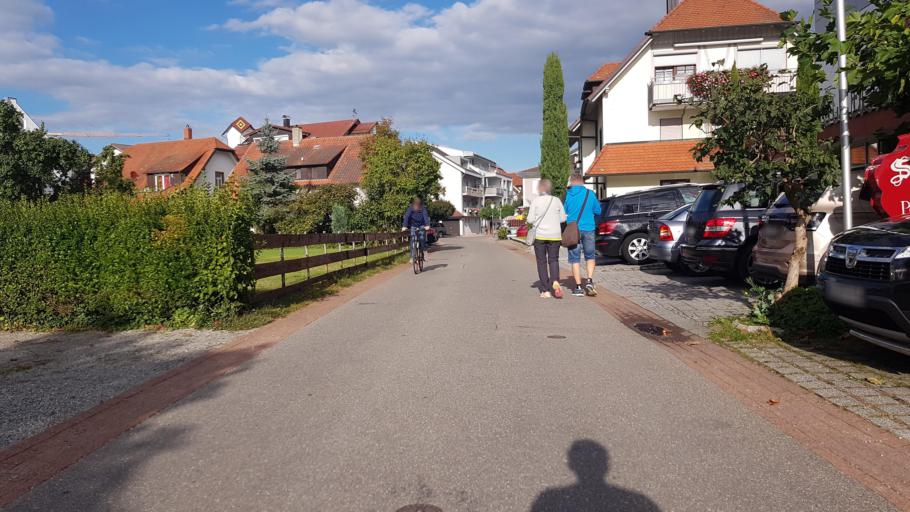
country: DE
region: Baden-Wuerttemberg
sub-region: Tuebingen Region
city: Immenstaad am Bodensee
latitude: 47.6631
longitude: 9.3635
